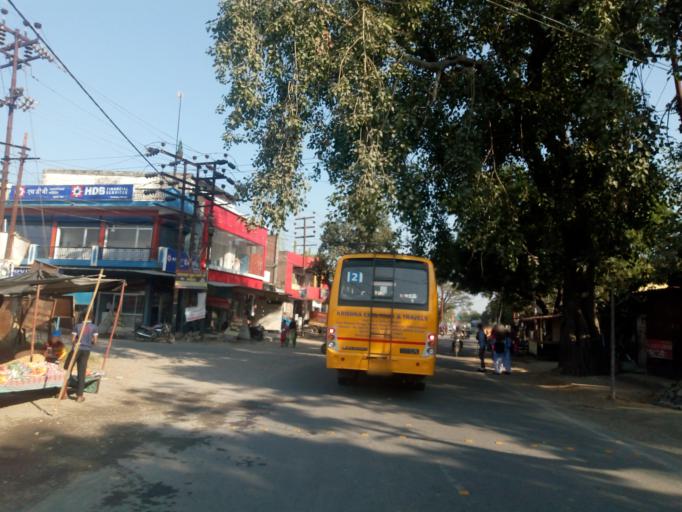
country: IN
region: Uttarakhand
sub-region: Dehradun
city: Harbatpur
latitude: 30.4407
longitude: 77.7329
